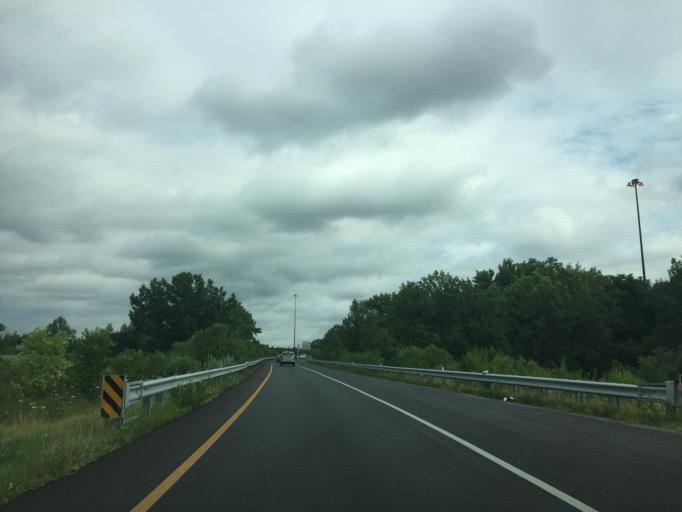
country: US
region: Maryland
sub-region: Baltimore County
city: Rosedale
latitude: 39.2943
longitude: -76.5029
